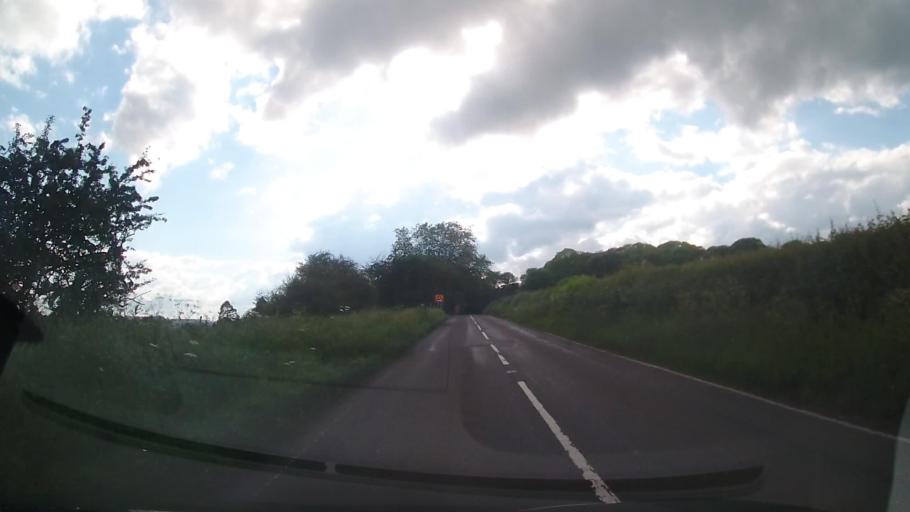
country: GB
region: England
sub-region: Shropshire
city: Much Wenlock
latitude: 52.6415
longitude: -2.5613
